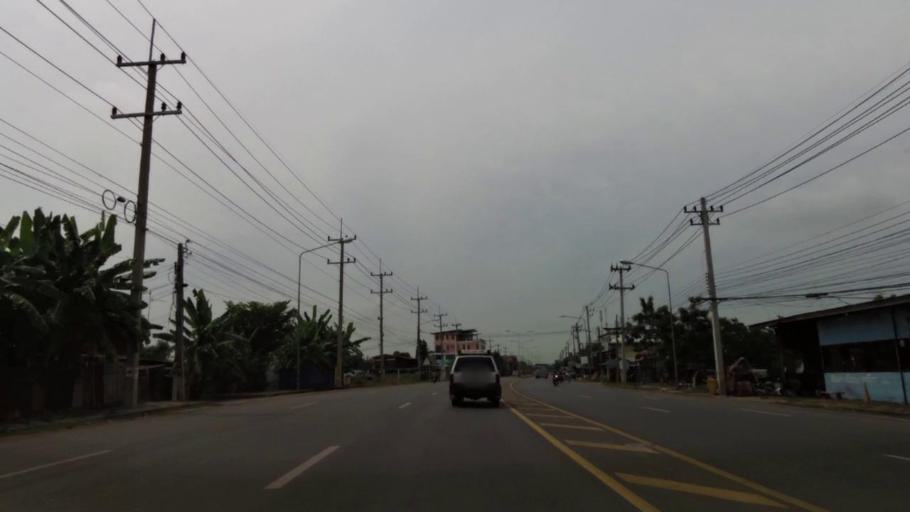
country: TH
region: Lop Buri
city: Ban Mi
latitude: 15.0507
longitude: 100.5739
